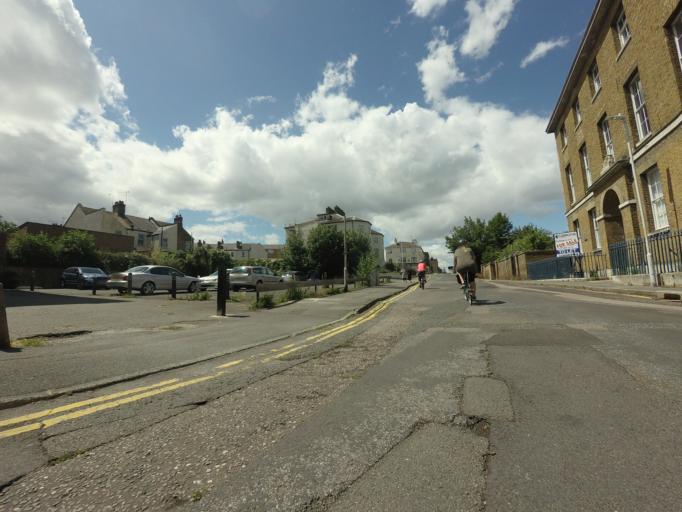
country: GB
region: England
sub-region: Kent
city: Gravesend
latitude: 51.4436
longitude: 0.3759
